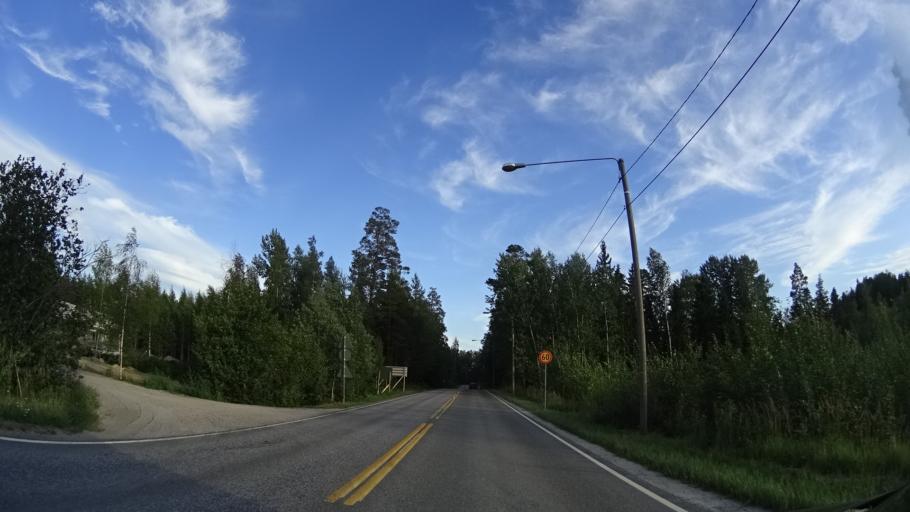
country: FI
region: Uusimaa
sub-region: Helsinki
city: Kirkkonummi
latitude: 60.2111
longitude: 24.4870
